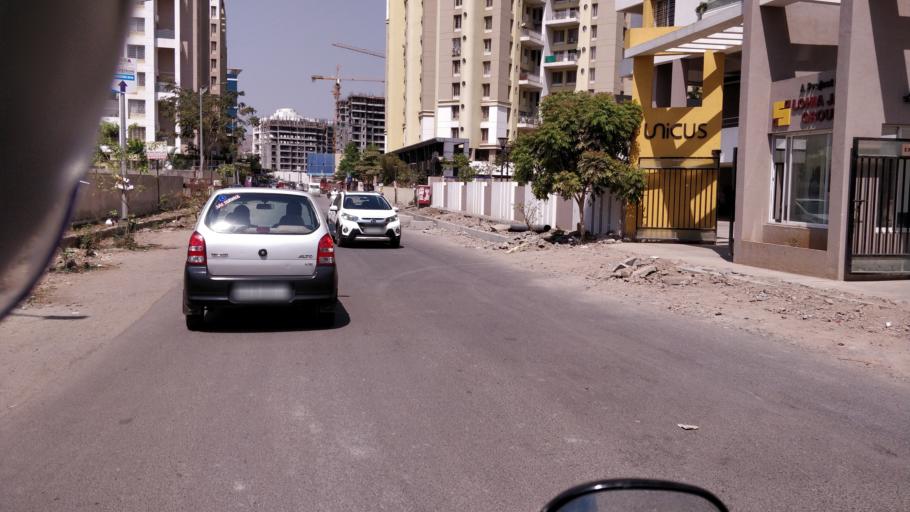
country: IN
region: Maharashtra
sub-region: Pune Division
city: Kharakvasla
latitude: 18.5112
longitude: 73.7767
